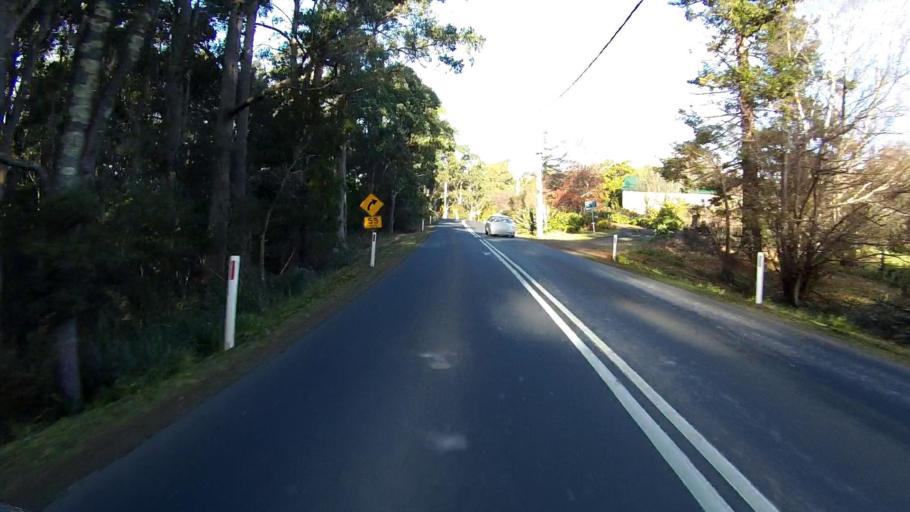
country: AU
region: Tasmania
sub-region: Clarence
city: Sandford
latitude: -43.1346
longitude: 147.8502
